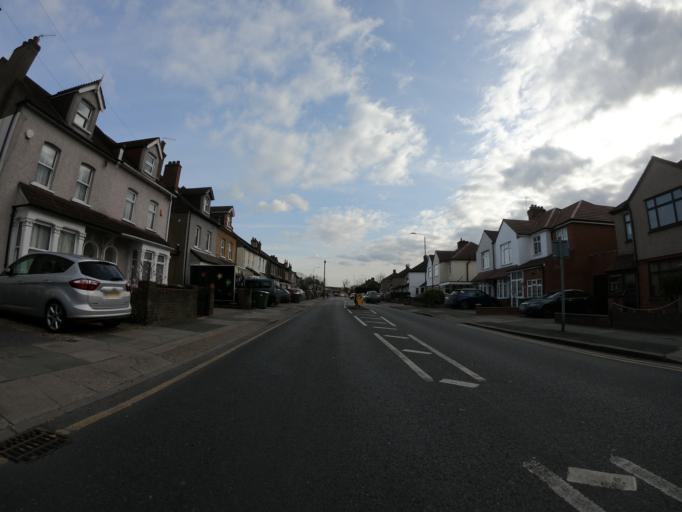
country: GB
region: England
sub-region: Greater London
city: Bexleyheath
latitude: 51.4649
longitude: 0.1403
